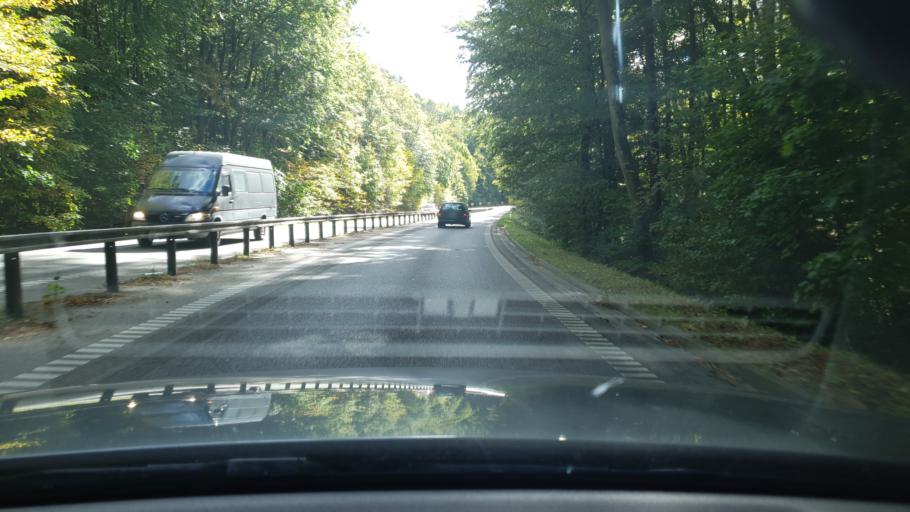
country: PL
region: Pomeranian Voivodeship
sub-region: Powiat wejherowski
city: Rekowo Dolne
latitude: 54.6297
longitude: 18.3445
